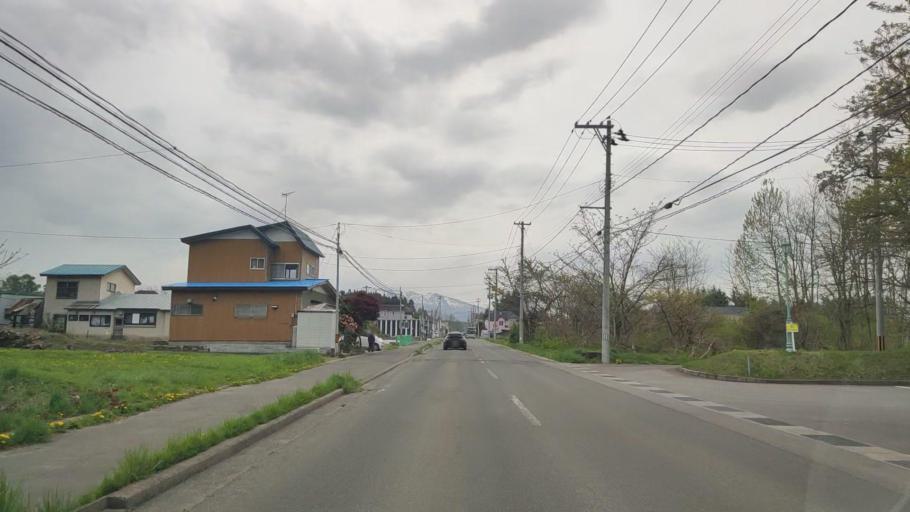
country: JP
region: Aomori
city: Aomori Shi
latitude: 40.7845
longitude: 140.7903
